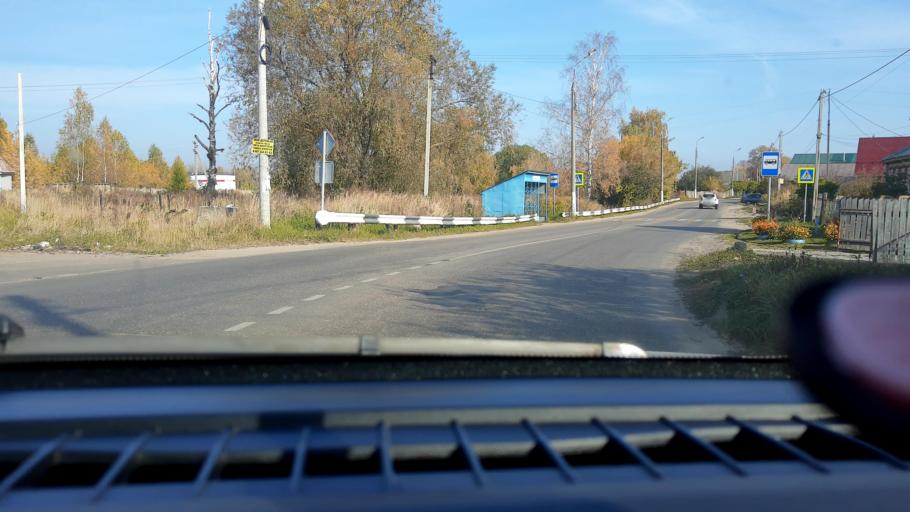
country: RU
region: Nizjnij Novgorod
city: Kstovo
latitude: 56.1526
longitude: 44.2321
